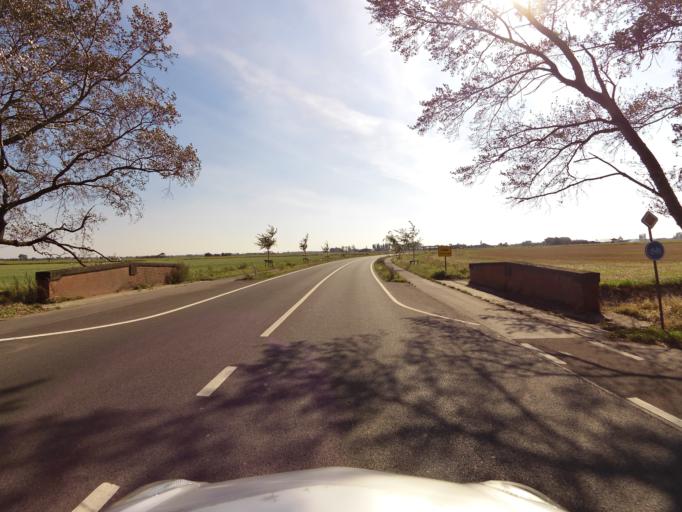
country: BE
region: Flanders
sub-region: Provincie West-Vlaanderen
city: Gistel
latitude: 51.1161
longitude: 2.8904
